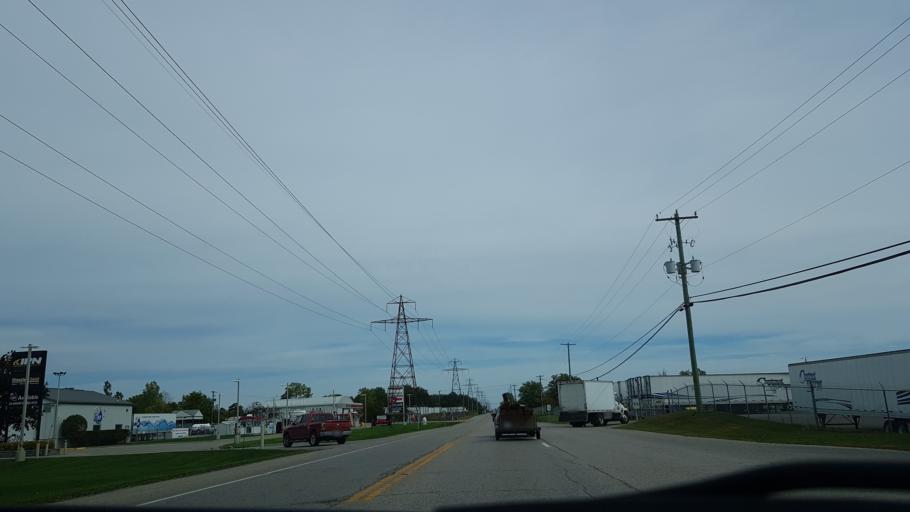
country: CA
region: Ontario
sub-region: Wellington County
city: Guelph
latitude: 43.4944
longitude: -80.2799
